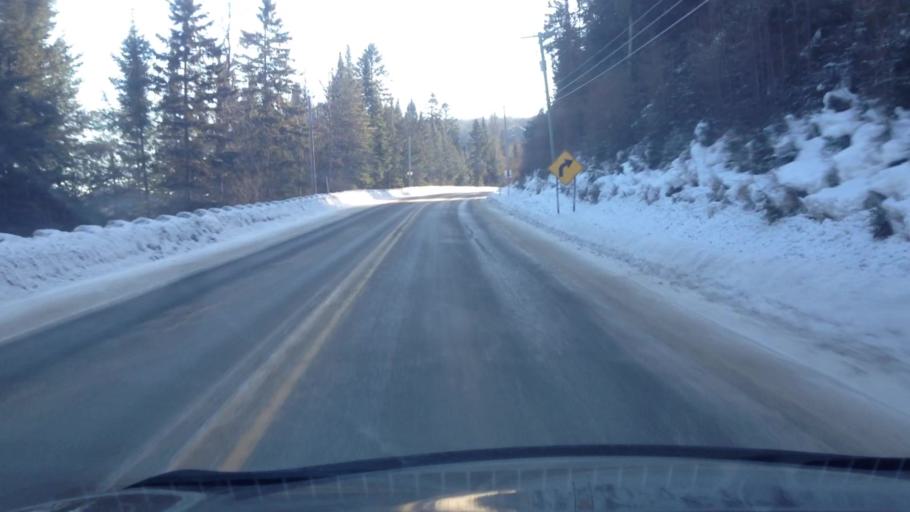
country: CA
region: Quebec
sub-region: Laurentides
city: Sainte-Agathe-des-Monts
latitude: 45.9180
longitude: -74.3757
